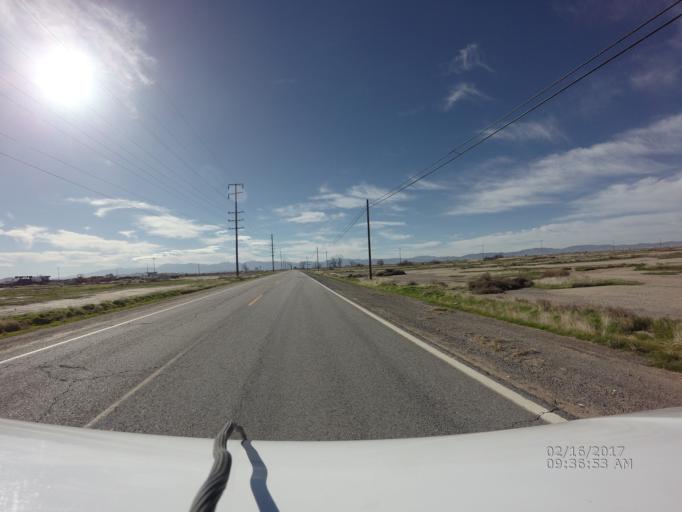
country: US
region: California
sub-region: Los Angeles County
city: Lancaster
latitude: 34.7430
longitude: -117.9699
